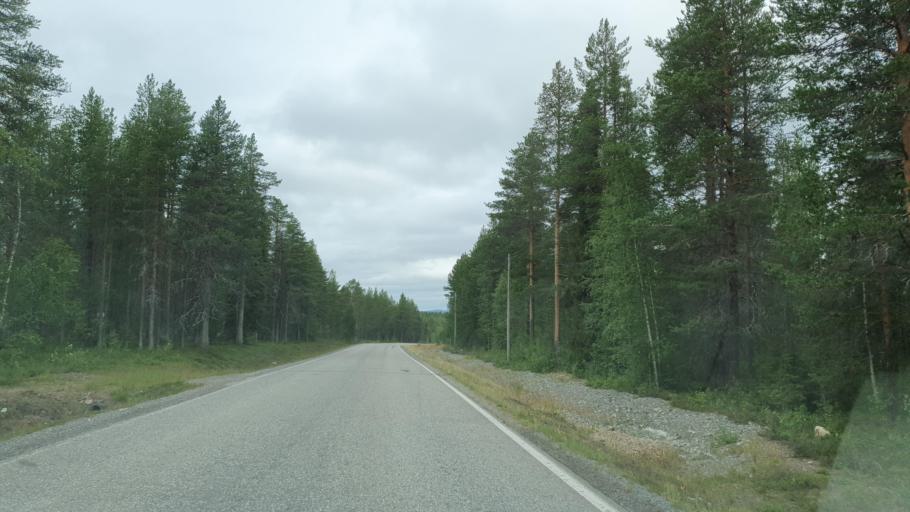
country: FI
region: Lapland
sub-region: Pohjois-Lappi
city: Sodankylae
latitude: 67.4161
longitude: 26.2563
